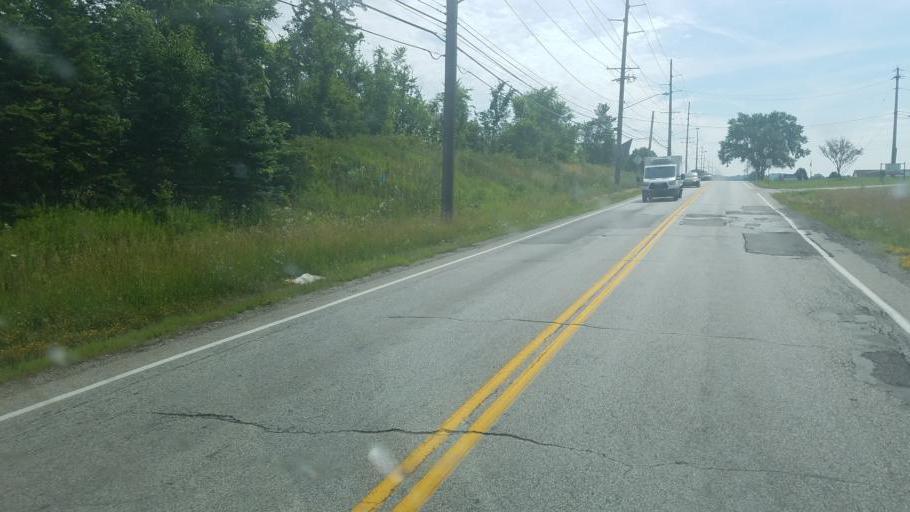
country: US
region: Ohio
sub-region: Cuyahoga County
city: North Royalton
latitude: 41.3162
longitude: -81.7788
